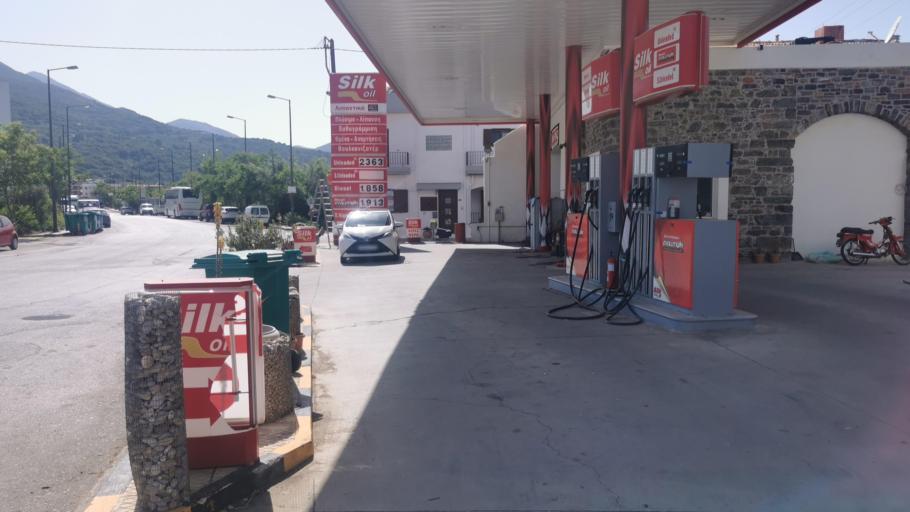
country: GR
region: Crete
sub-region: Nomos Lasithiou
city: Neapoli
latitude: 35.2587
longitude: 25.6062
